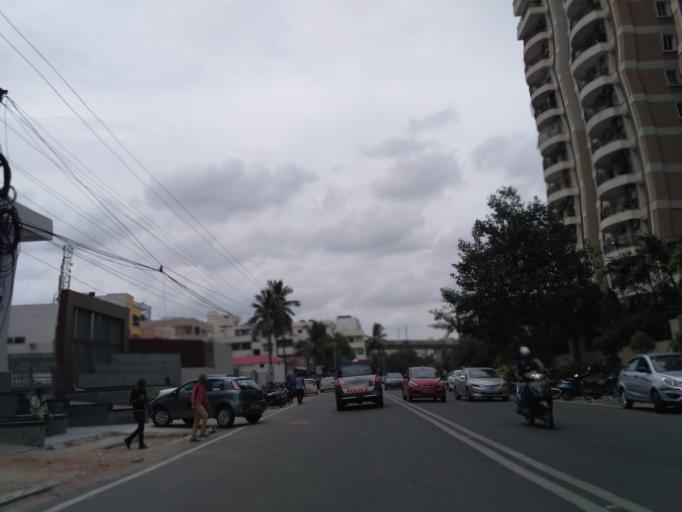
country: IN
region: Telangana
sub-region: Rangareddi
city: Kukatpalli
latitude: 17.4391
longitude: 78.3891
